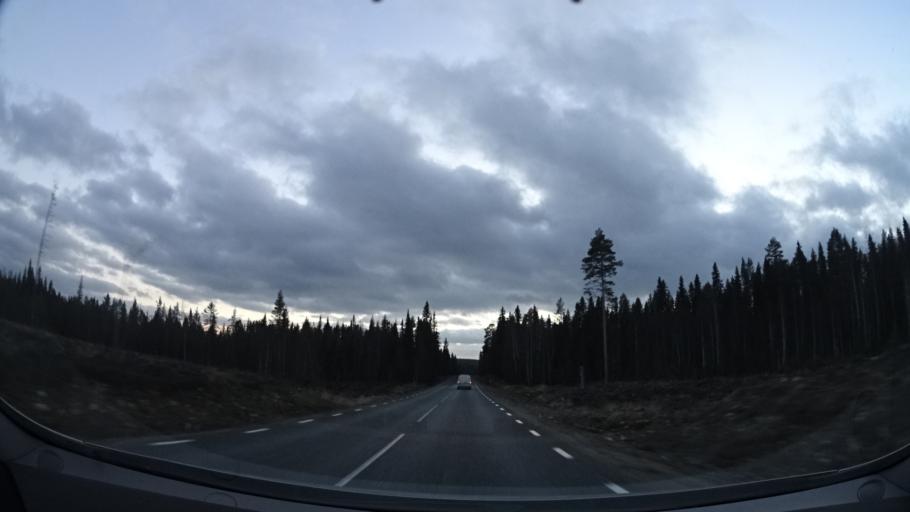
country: SE
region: Vaesterbotten
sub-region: Asele Kommun
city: Insjon
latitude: 64.2836
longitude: 17.6146
